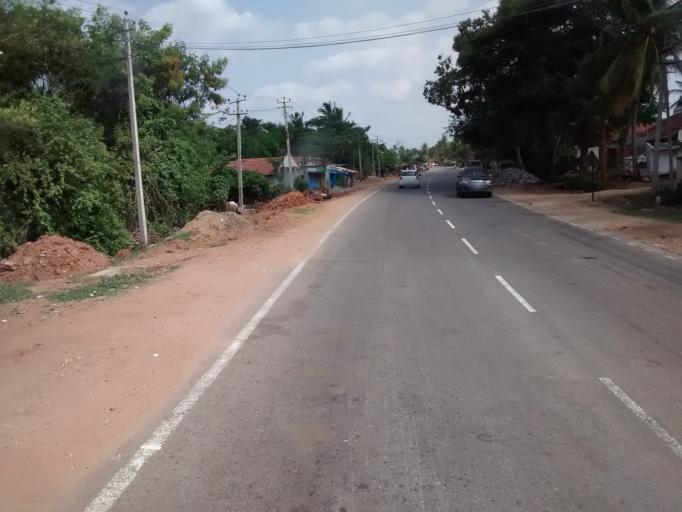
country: IN
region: Karnataka
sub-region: Mysore
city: Hunsur
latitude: 12.3701
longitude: 76.4173
